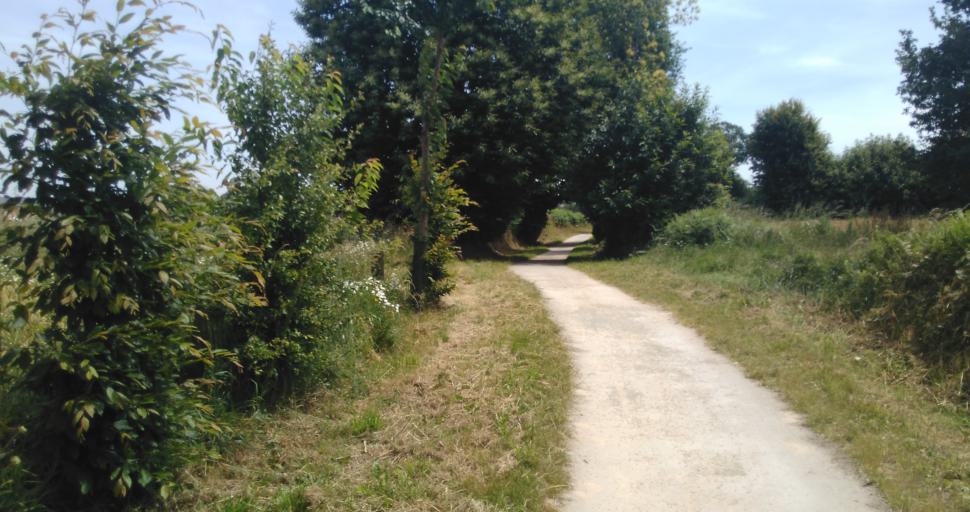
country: FR
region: Brittany
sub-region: Departement d'Ille-et-Vilaine
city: La Meziere
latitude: 48.2197
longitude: -1.7692
